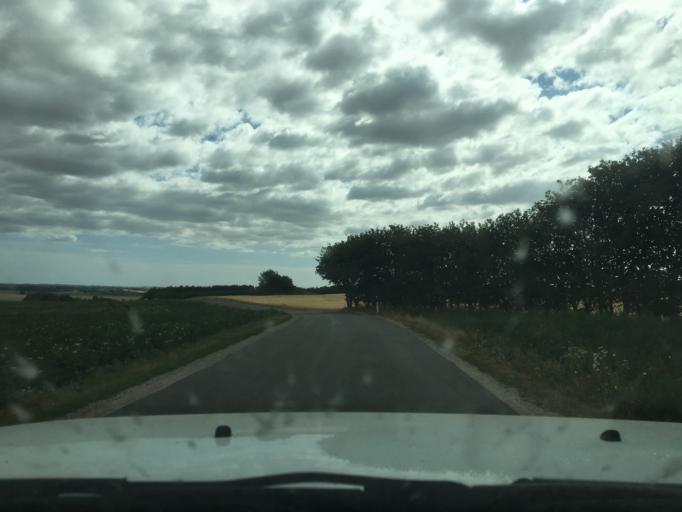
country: DK
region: Central Jutland
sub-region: Syddjurs Kommune
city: Ryomgard
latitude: 56.3954
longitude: 10.6437
